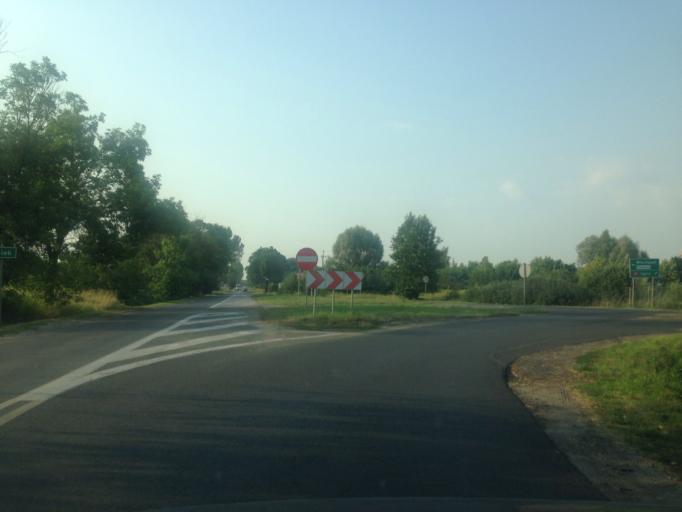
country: PL
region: Kujawsko-Pomorskie
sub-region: Powiat wloclawski
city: Fabianki
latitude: 52.6905
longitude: 19.1042
